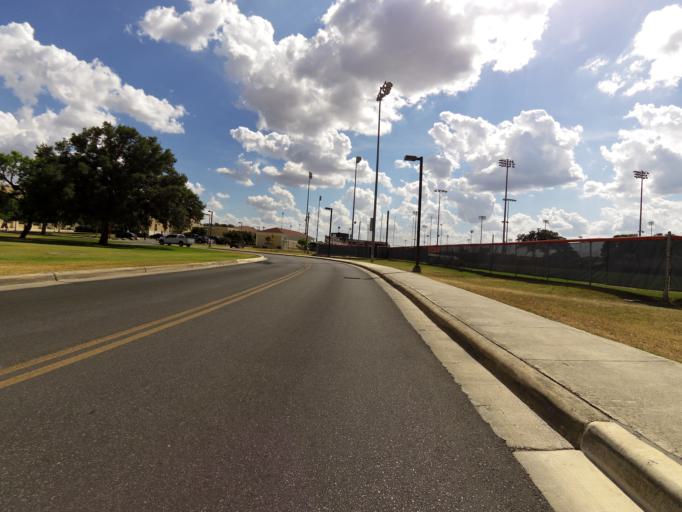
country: US
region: Texas
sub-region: Bexar County
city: Helotes
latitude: 29.5831
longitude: -98.6224
